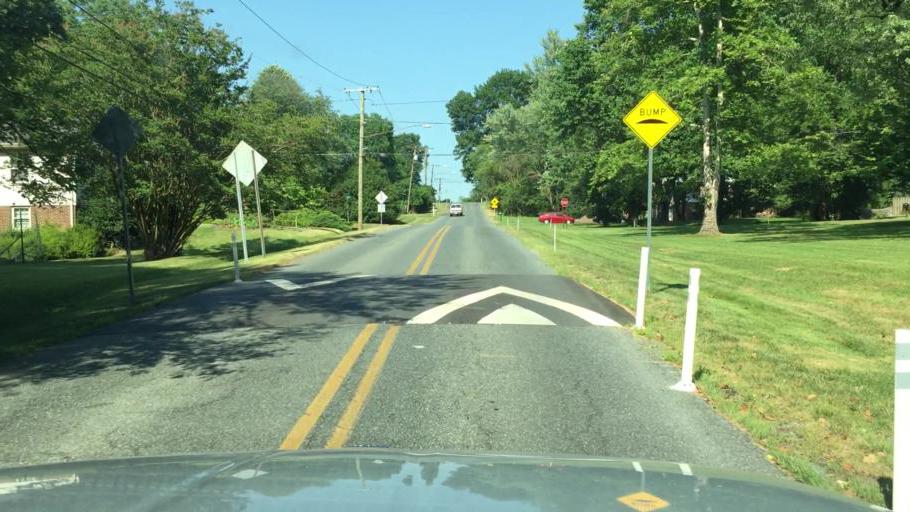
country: US
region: Maryland
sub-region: Montgomery County
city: Colesville
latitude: 39.0671
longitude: -77.0075
